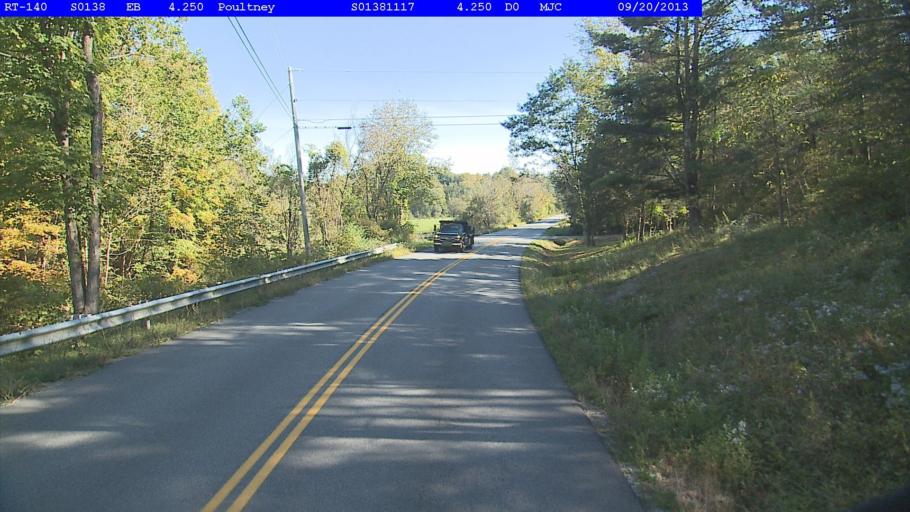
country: US
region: Vermont
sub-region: Rutland County
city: Poultney
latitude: 43.5050
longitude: -73.1763
